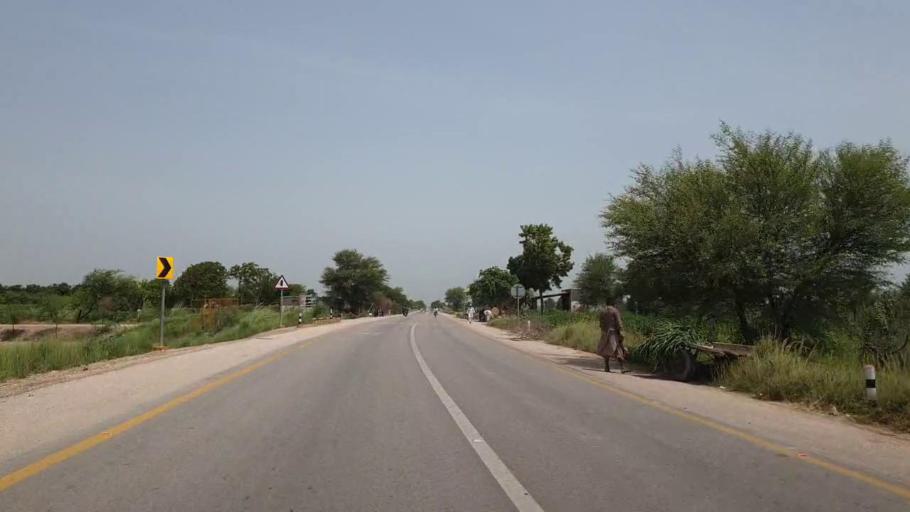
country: PK
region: Sindh
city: Shahpur Chakar
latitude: 26.1499
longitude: 68.6364
